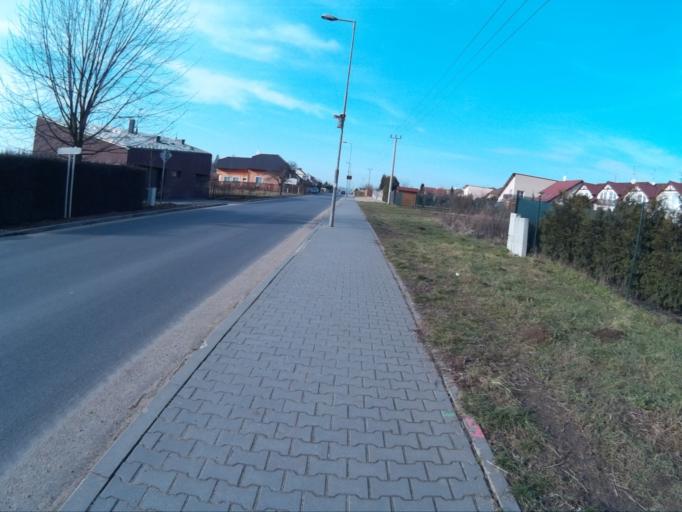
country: CZ
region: South Moravian
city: Troubsko
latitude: 49.1651
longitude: 16.5226
